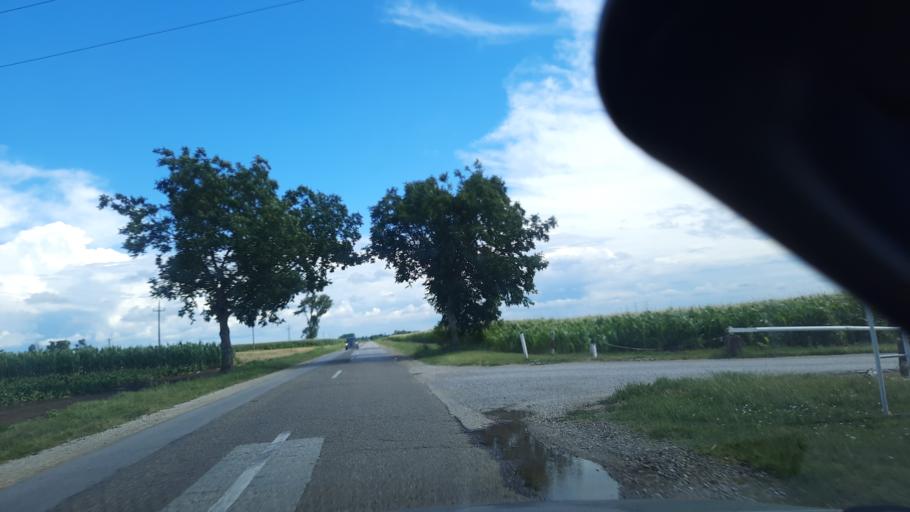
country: RS
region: Autonomna Pokrajina Vojvodina
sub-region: Sremski Okrug
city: Sremska Mitrovica
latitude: 45.0480
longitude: 19.6058
